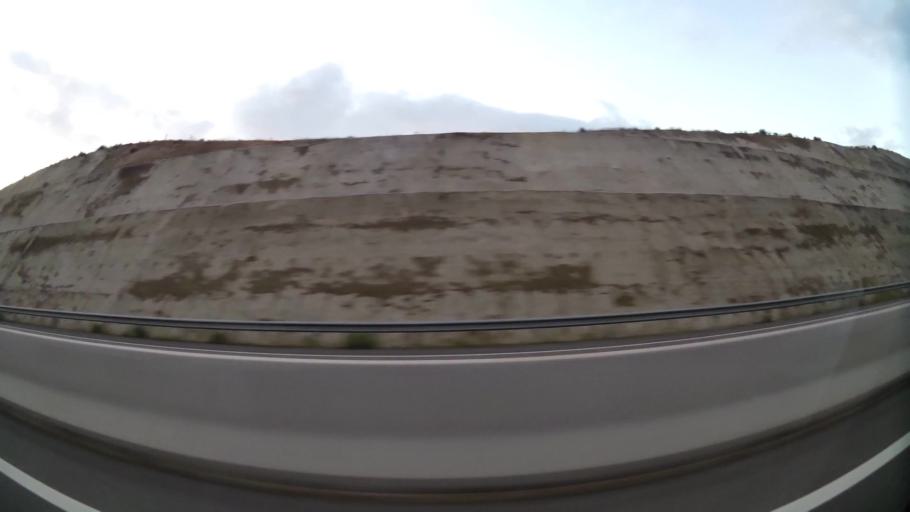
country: MA
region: Oriental
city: El Aioun
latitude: 34.5955
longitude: -2.6523
